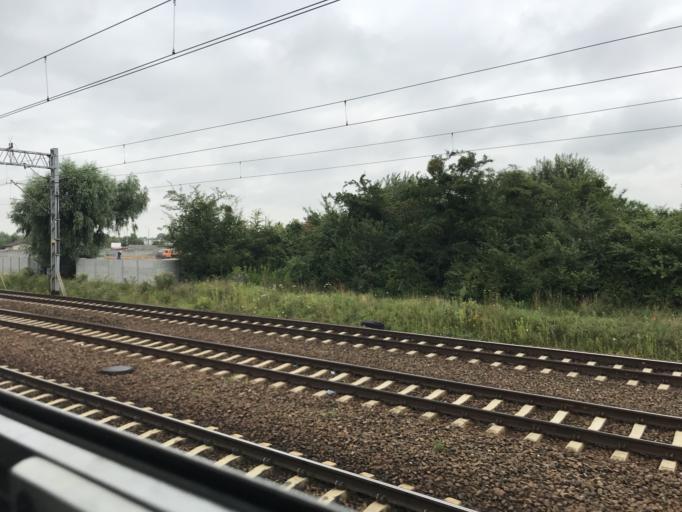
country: PL
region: Pomeranian Voivodeship
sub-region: Powiat gdanski
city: Pruszcz Gdanski
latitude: 54.2509
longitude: 18.6470
